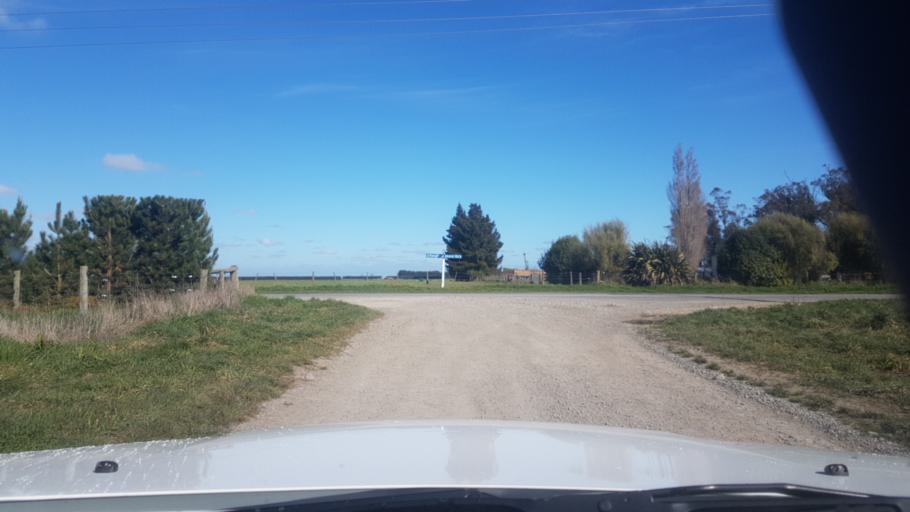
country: NZ
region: Canterbury
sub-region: Ashburton District
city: Tinwald
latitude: -44.1027
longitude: 171.4494
